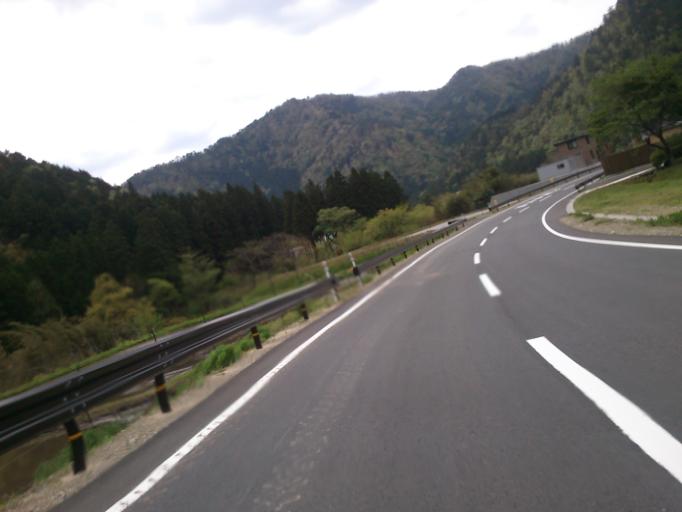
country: JP
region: Fukui
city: Obama
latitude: 35.2965
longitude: 135.6123
